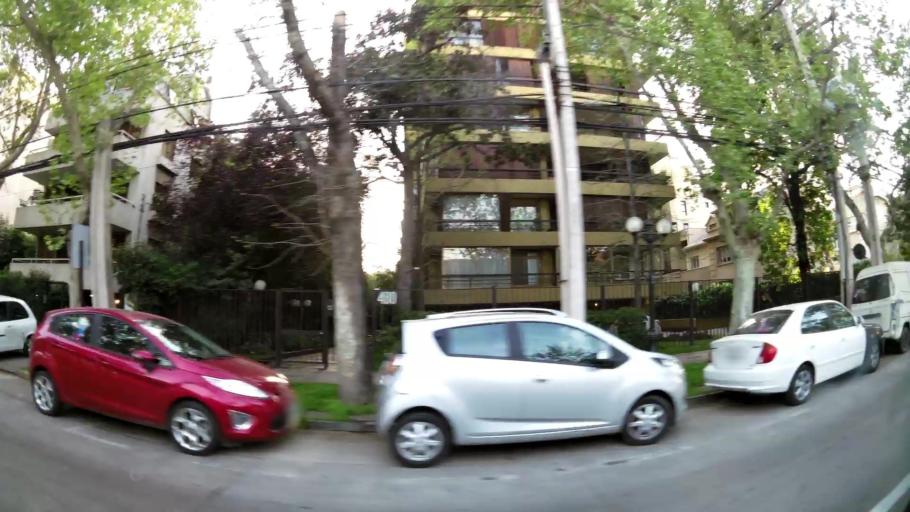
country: CL
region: Santiago Metropolitan
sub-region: Provincia de Santiago
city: Villa Presidente Frei, Nunoa, Santiago, Chile
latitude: -33.4235
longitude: -70.6025
